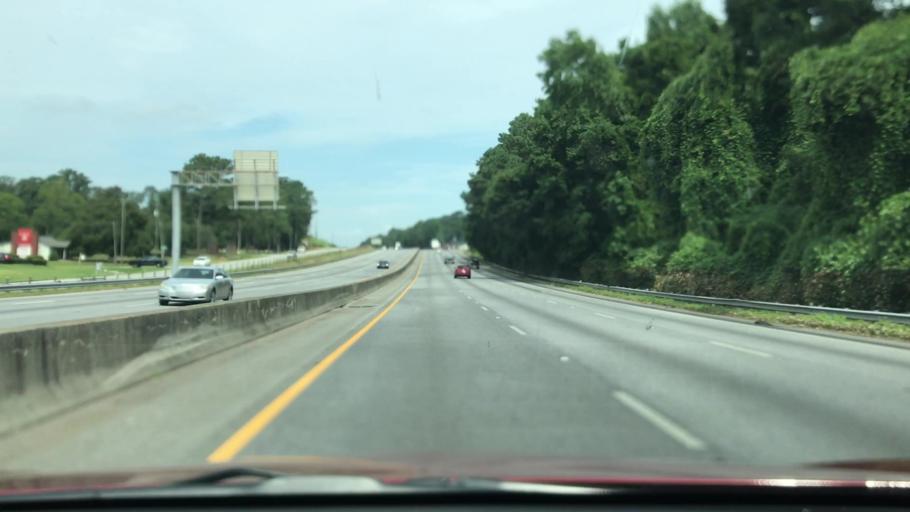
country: US
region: Georgia
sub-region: Newton County
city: Oxford
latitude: 33.6104
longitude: -83.8866
